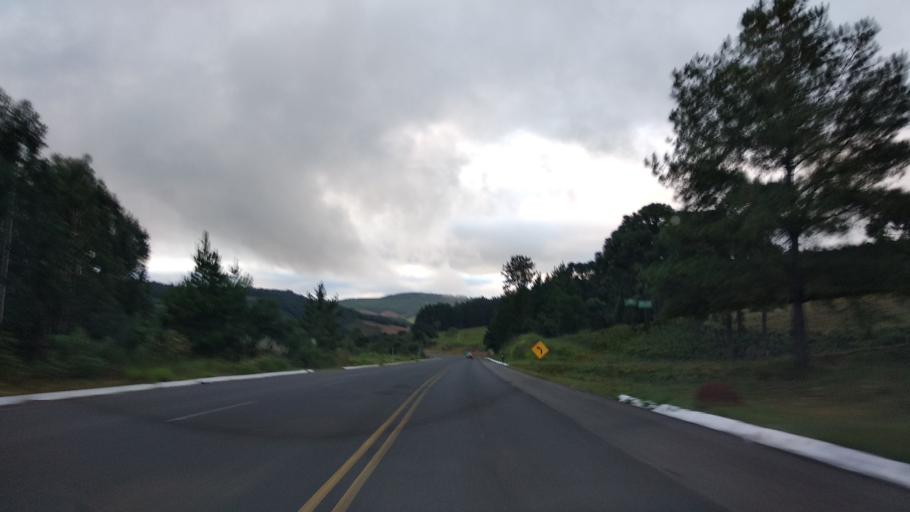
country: BR
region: Santa Catarina
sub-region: Campos Novos
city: Campos Novos
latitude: -27.4487
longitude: -50.9965
